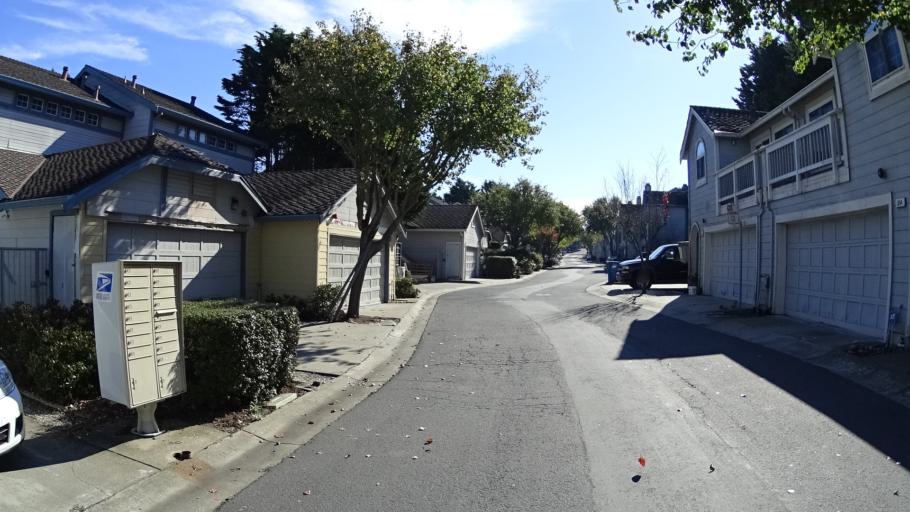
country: US
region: California
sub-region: San Mateo County
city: Colma
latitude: 37.6559
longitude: -122.4603
